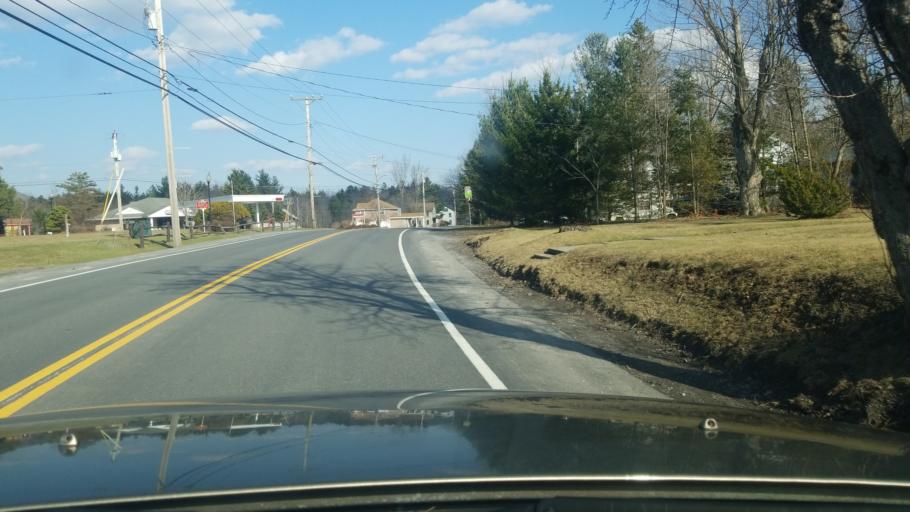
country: US
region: New York
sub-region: Ulster County
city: Manorville
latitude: 42.1971
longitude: -74.1096
